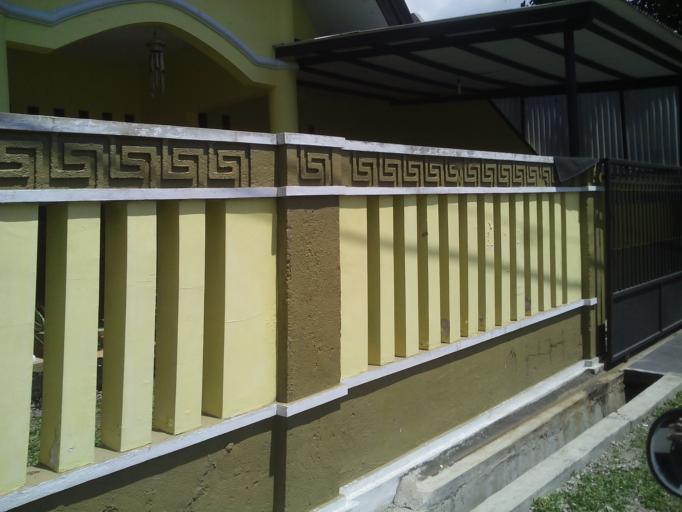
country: ID
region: East Java
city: Sumbersari Wetan
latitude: -8.1786
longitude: 113.7176
